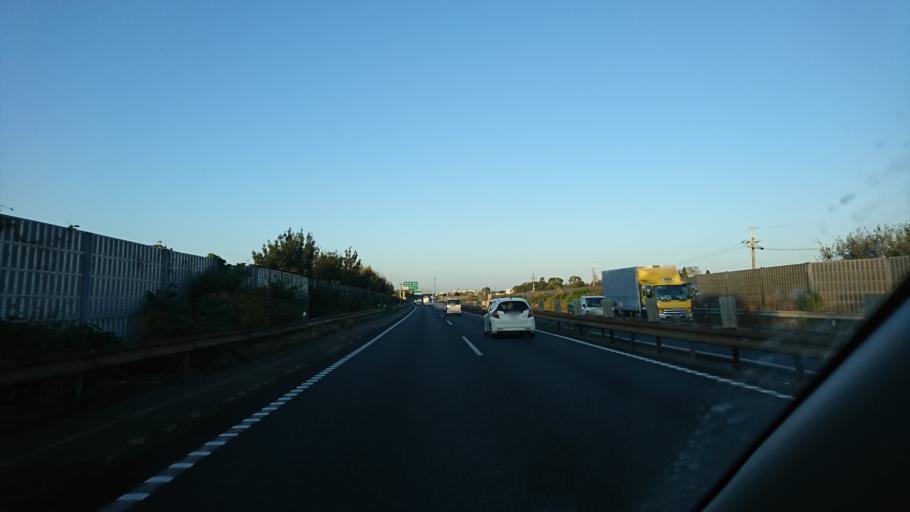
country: JP
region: Hyogo
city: Kakogawacho-honmachi
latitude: 34.7165
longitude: 134.9117
